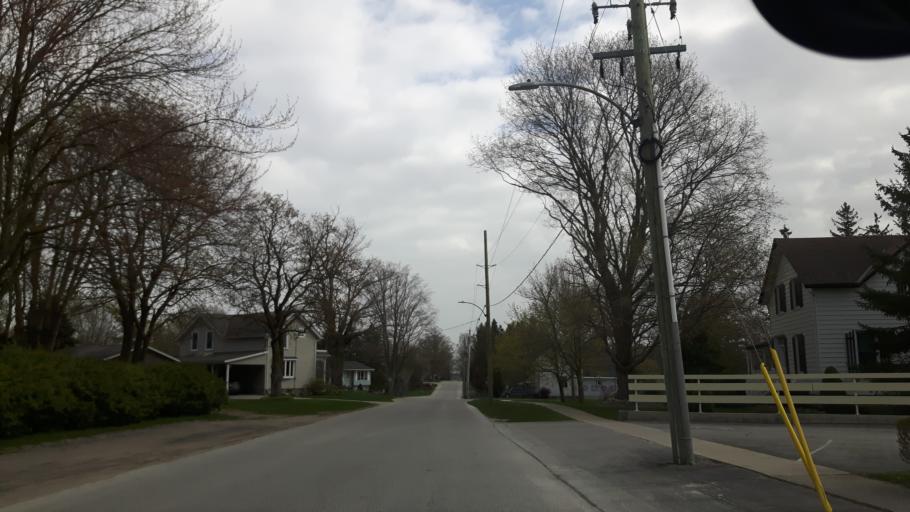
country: CA
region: Ontario
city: Bluewater
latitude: 43.6193
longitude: -81.5451
